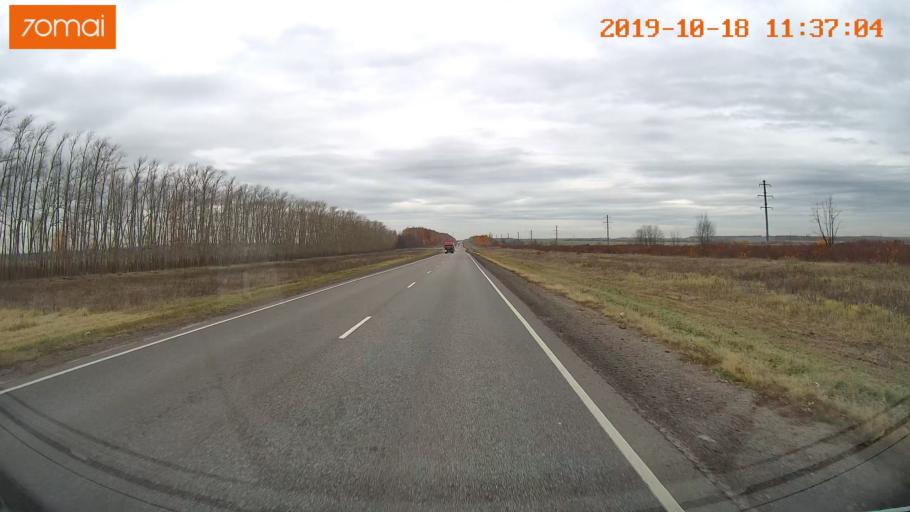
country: RU
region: Rjazan
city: Oktyabr'skiy
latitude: 54.1476
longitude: 38.8214
